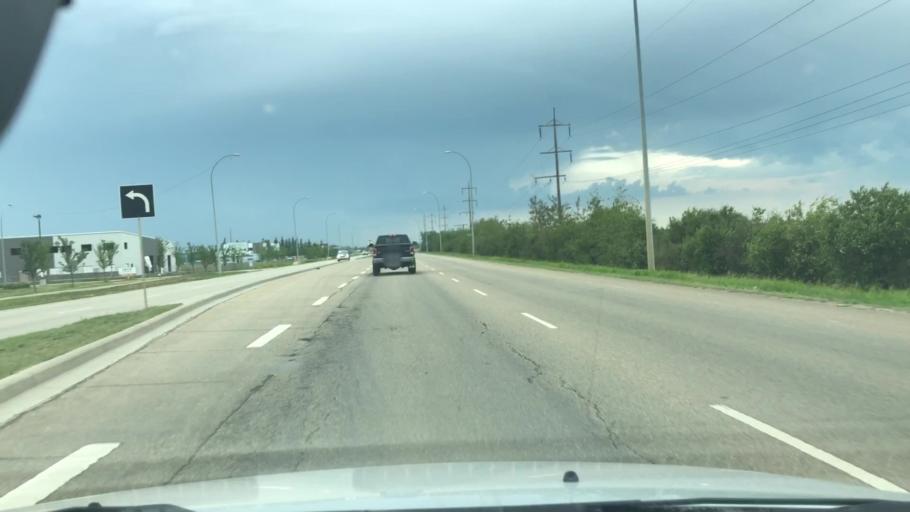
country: CA
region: Alberta
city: St. Albert
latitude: 53.5995
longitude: -113.5950
